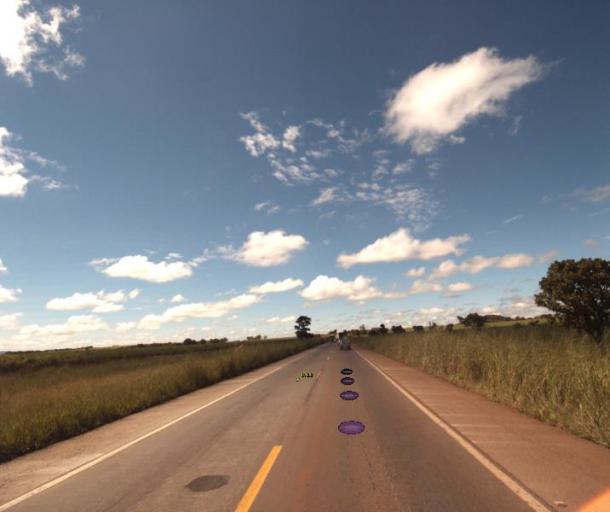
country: BR
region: Goias
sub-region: Rialma
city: Rialma
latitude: -15.4139
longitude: -49.5248
